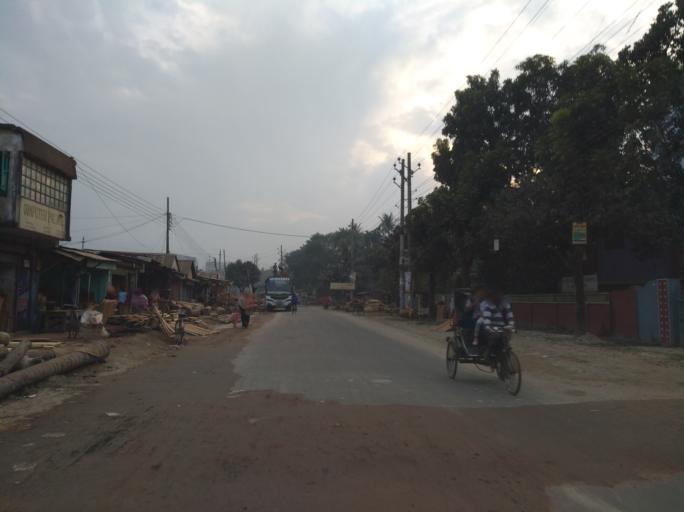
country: BD
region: Khulna
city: Khulna
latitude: 22.8471
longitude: 89.5419
